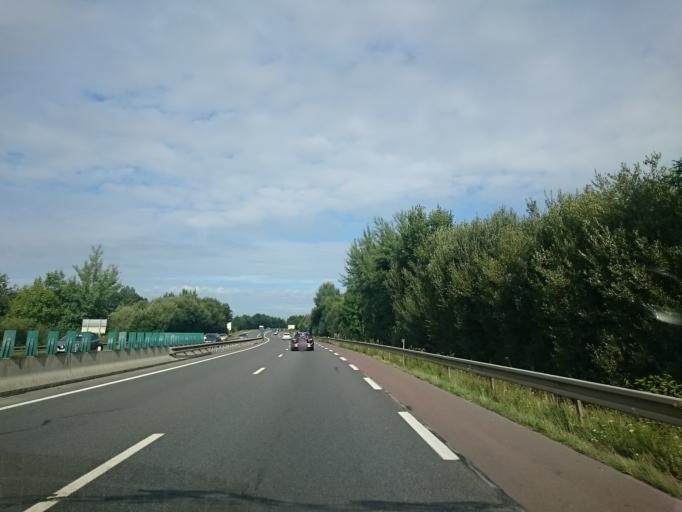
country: FR
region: Lower Normandy
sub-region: Departement de la Manche
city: Le Val-Saint-Pere
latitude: 48.6567
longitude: -1.3575
